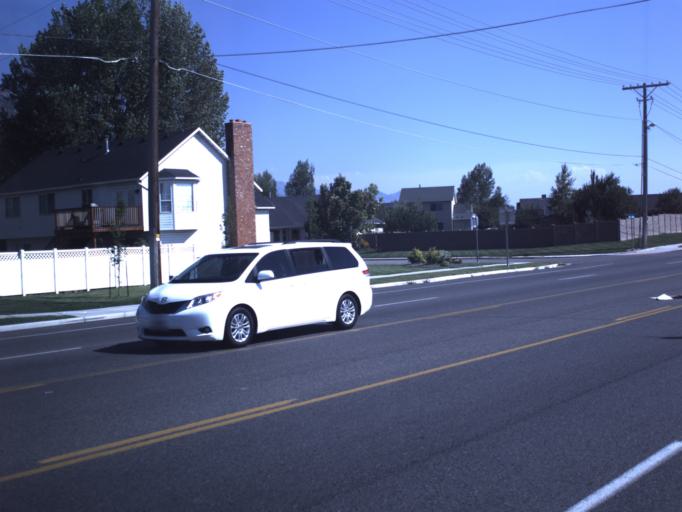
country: US
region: Utah
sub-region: Utah County
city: Highland
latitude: 40.4307
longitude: -111.7736
